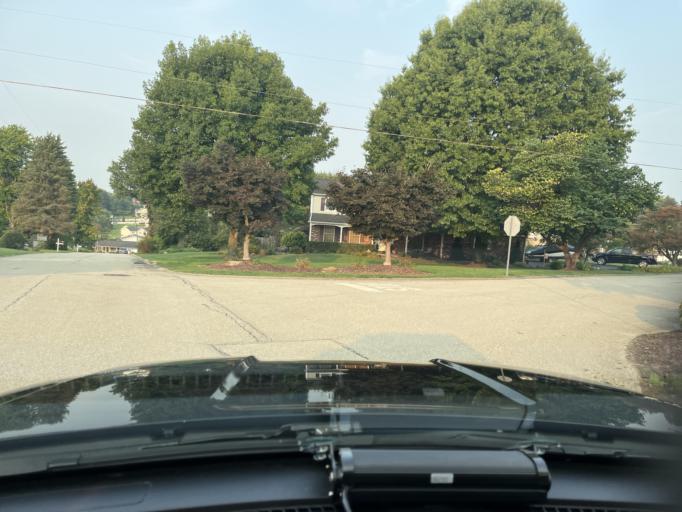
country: US
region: Pennsylvania
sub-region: Fayette County
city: South Uniontown
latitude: 39.8962
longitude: -79.7589
